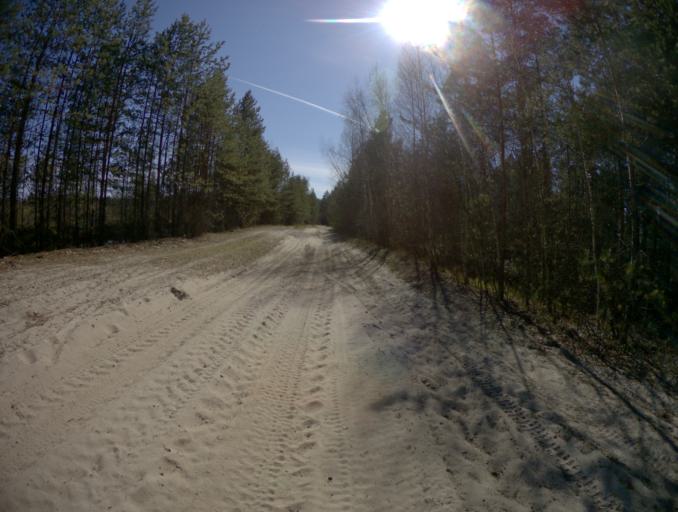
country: RU
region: Vladimir
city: Ivanishchi
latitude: 55.7646
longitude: 40.4099
